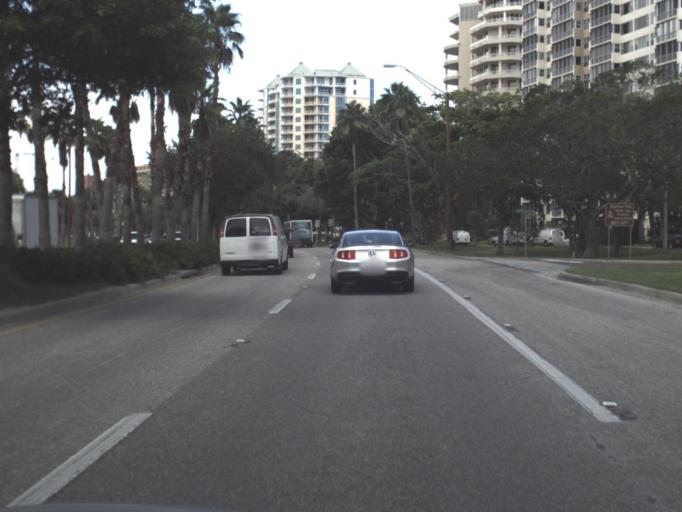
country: US
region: Florida
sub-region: Sarasota County
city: Sarasota
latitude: 27.3295
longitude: -82.5410
